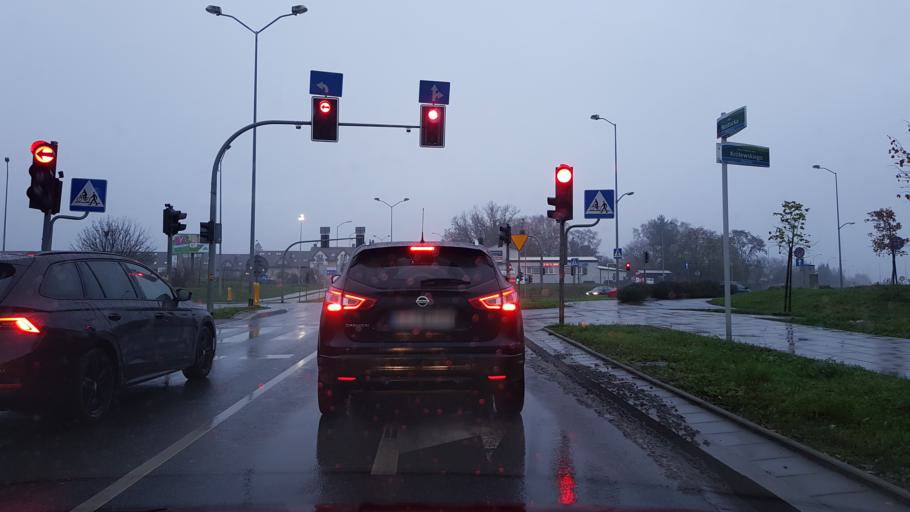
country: PL
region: West Pomeranian Voivodeship
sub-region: Szczecin
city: Szczecin
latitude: 53.4616
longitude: 14.5554
